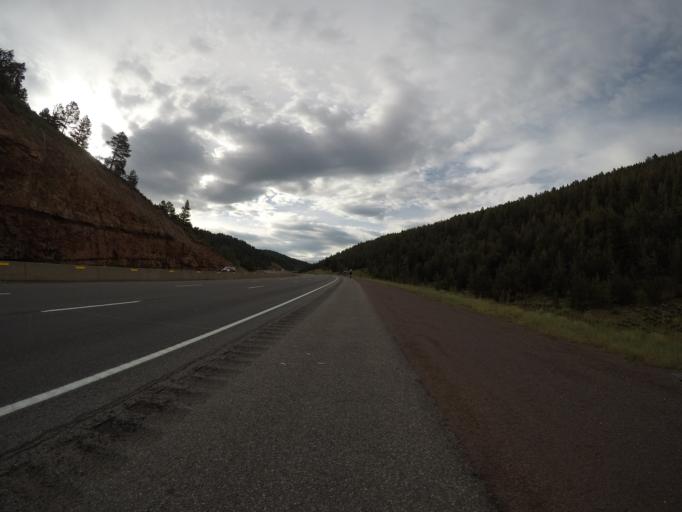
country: US
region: Wyoming
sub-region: Albany County
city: Laramie
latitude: 41.2633
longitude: -105.4645
